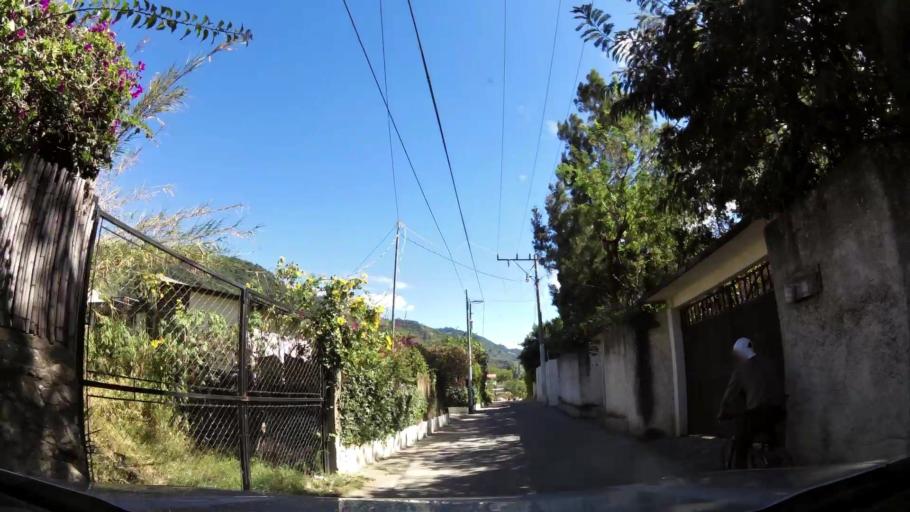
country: GT
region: Solola
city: Panajachel
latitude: 14.7385
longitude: -91.1563
